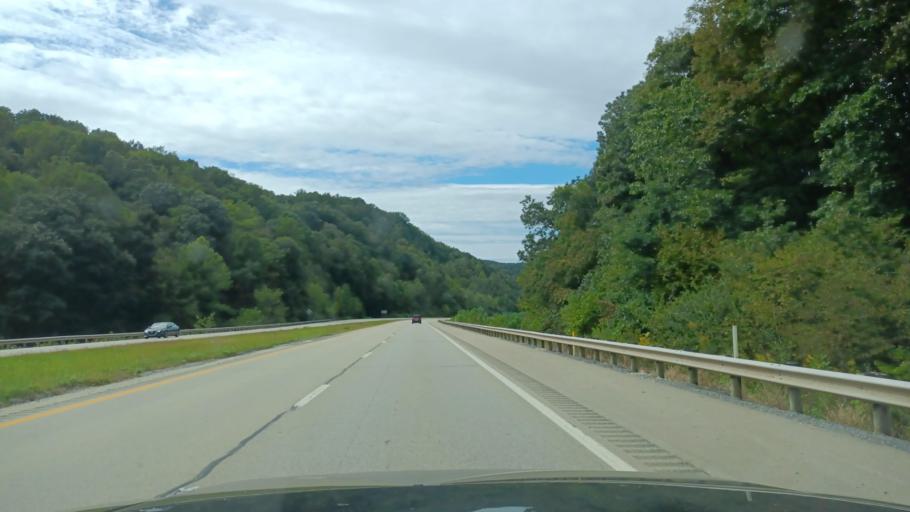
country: US
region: West Virginia
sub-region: Doddridge County
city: West Union
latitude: 39.2770
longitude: -80.7958
